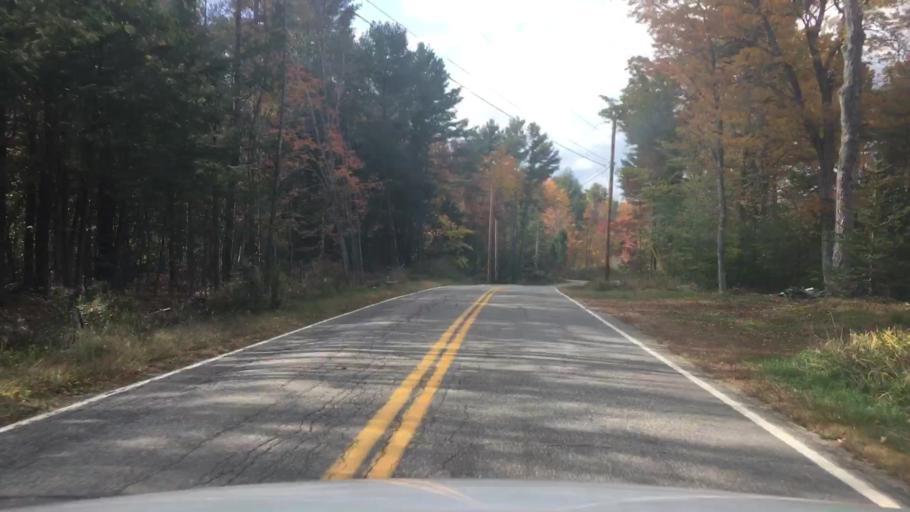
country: US
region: Maine
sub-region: Knox County
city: Washington
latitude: 44.3079
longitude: -69.3428
